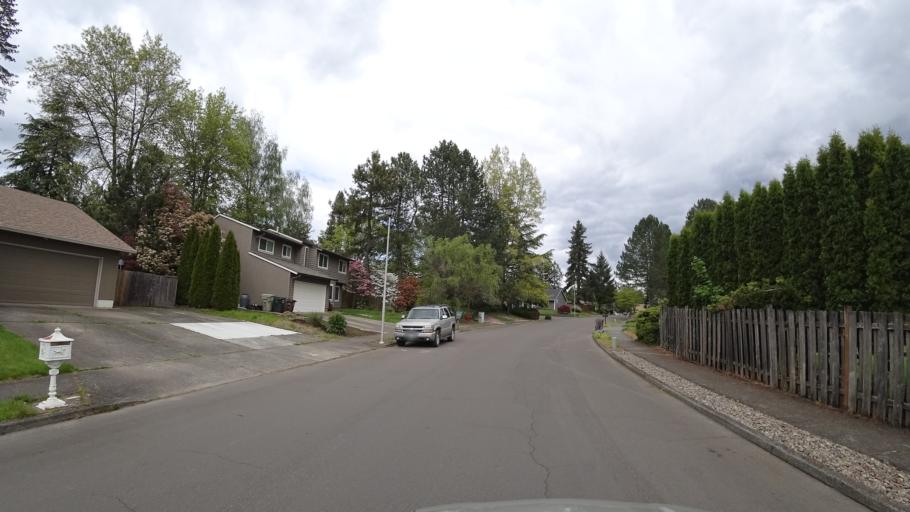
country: US
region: Oregon
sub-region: Washington County
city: Rockcreek
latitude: 45.5524
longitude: -122.8904
